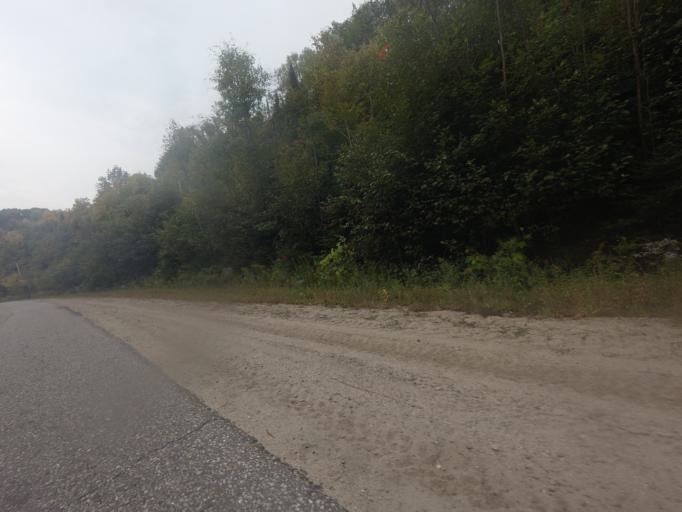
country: CA
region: Quebec
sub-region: Outaouais
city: Maniwaki
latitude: 46.0862
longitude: -76.0326
